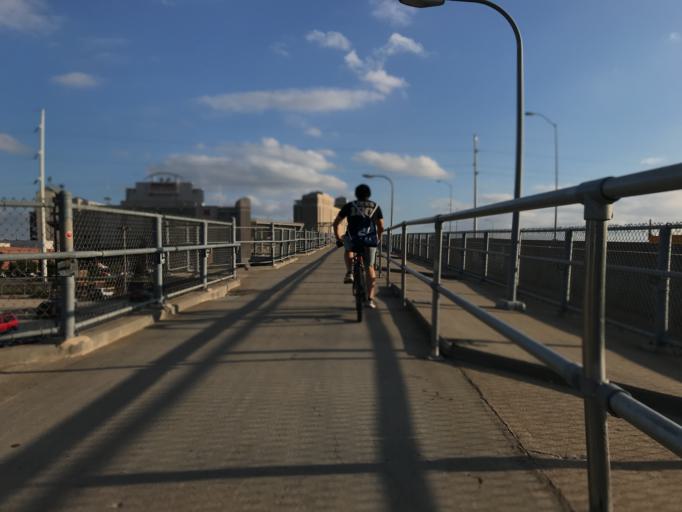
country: US
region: Nebraska
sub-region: Lancaster County
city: Lincoln
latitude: 40.8246
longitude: -96.7070
